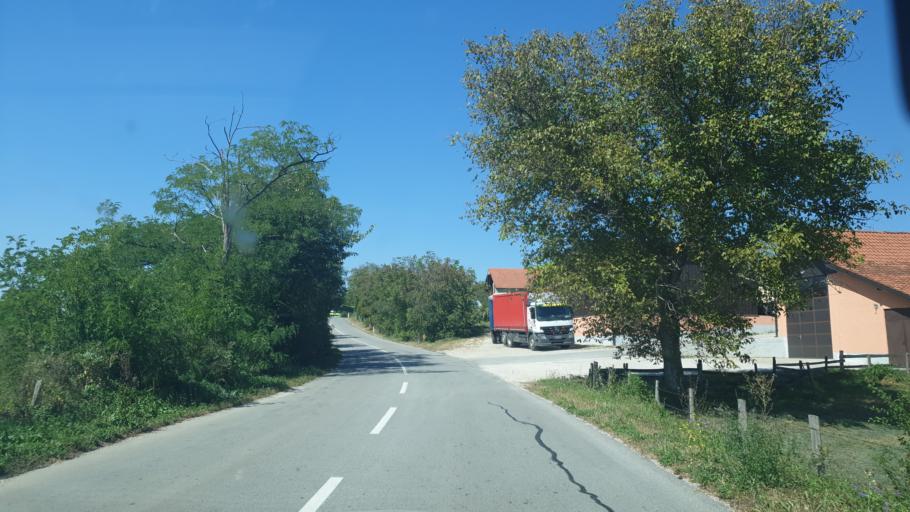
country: RS
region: Central Serbia
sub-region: Kolubarski Okrug
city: Mionica
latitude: 44.1891
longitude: 20.0324
